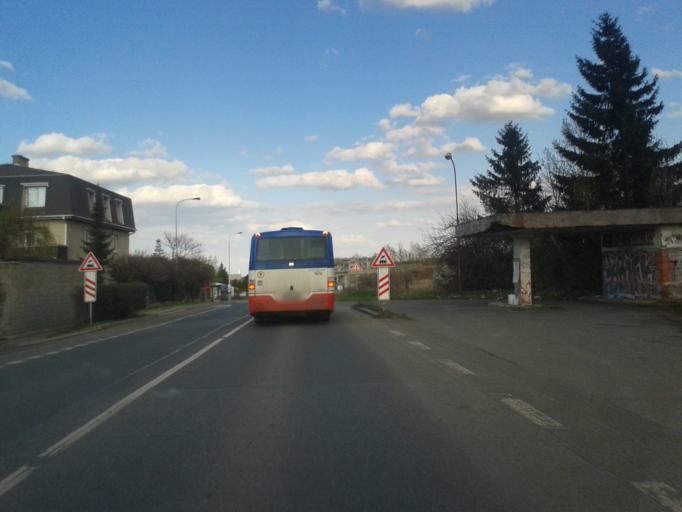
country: CZ
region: Central Bohemia
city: Hostivice
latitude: 50.0606
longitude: 14.3001
